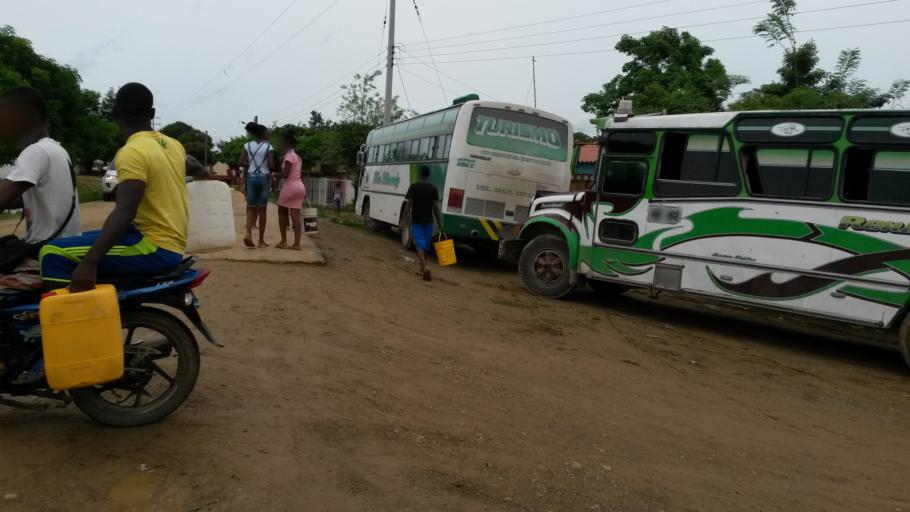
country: CO
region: Bolivar
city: San Pablo
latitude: 10.1060
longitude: -75.2007
